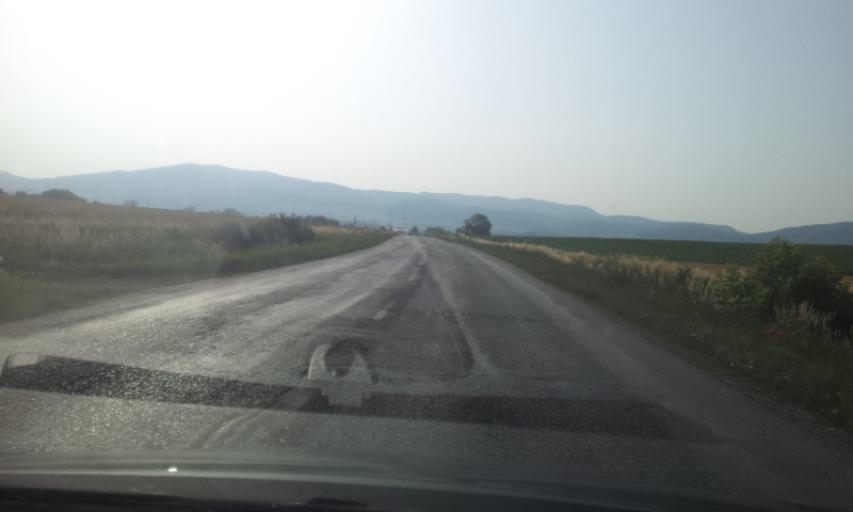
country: SK
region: Kosicky
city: Kosice
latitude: 48.6080
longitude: 21.2933
